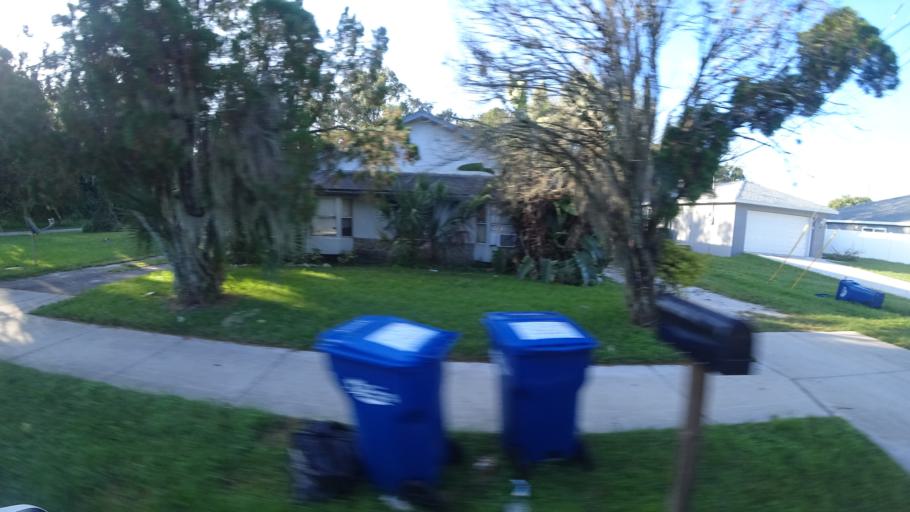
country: US
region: Florida
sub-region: Manatee County
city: Samoset
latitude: 27.4512
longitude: -82.5452
